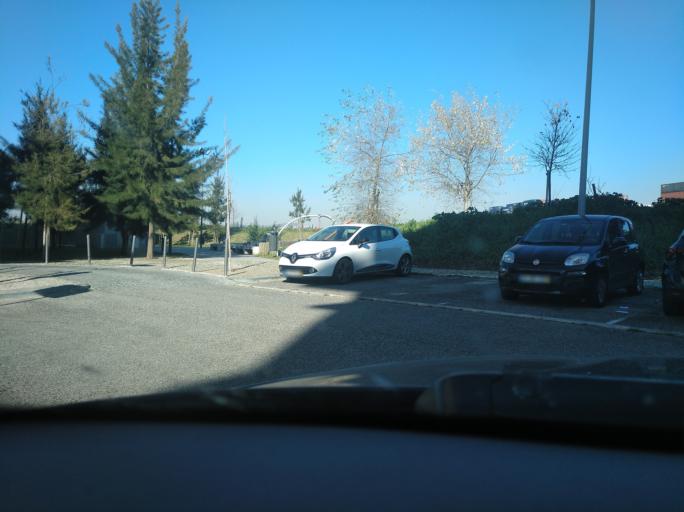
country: PT
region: Lisbon
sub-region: Odivelas
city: Pontinha
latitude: 38.7684
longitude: -9.1843
